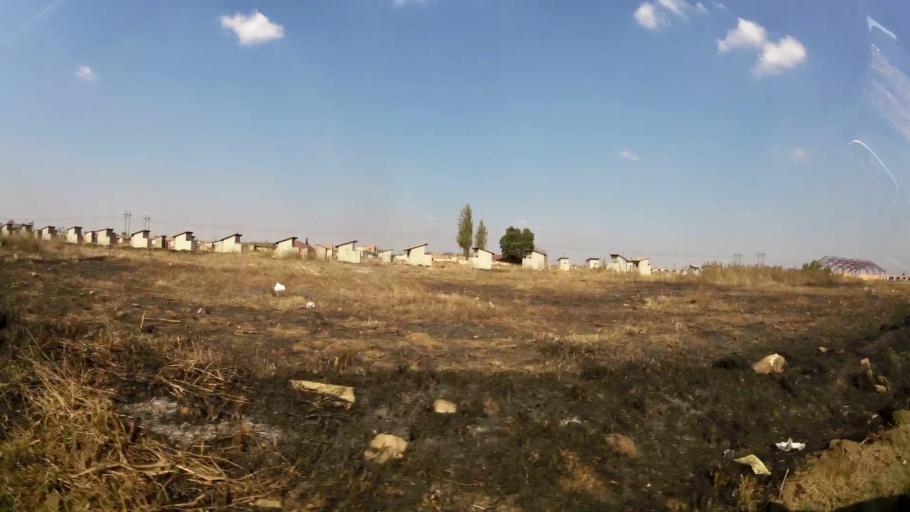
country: ZA
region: Gauteng
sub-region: Ekurhuleni Metropolitan Municipality
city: Benoni
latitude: -26.1402
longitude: 28.4069
